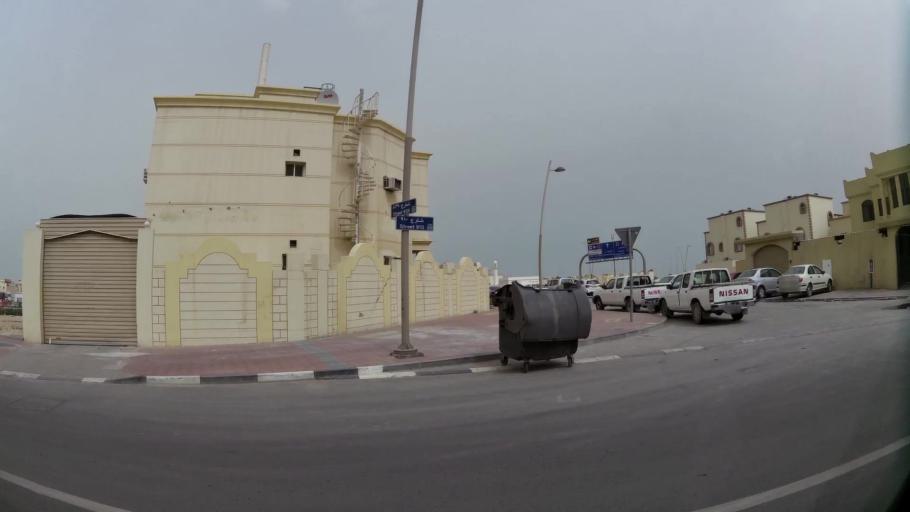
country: QA
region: Baladiyat ad Dawhah
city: Doha
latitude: 25.2294
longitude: 51.5543
